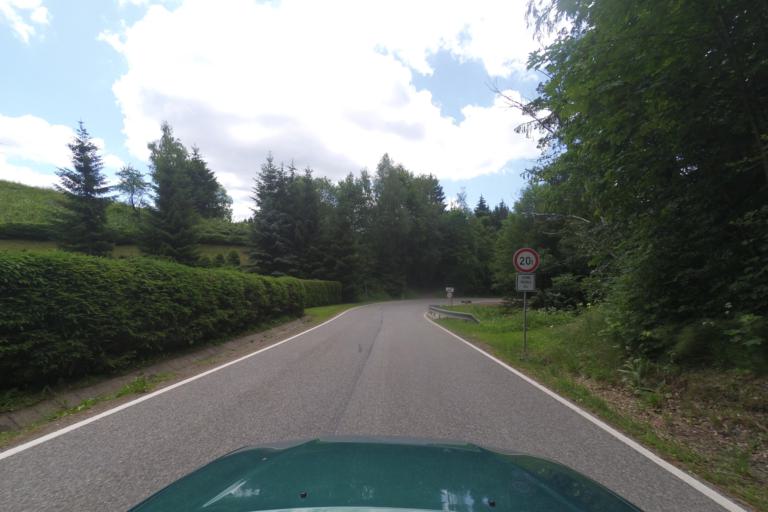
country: PL
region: Lower Silesian Voivodeship
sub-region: Powiat klodzki
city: Lewin Klodzki
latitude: 50.3527
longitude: 16.2443
